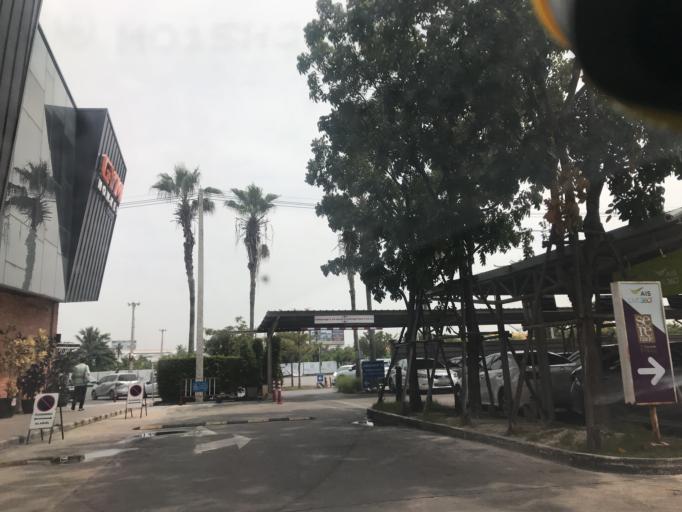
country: TH
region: Bangkok
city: Taling Chan
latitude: 13.7678
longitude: 100.4425
